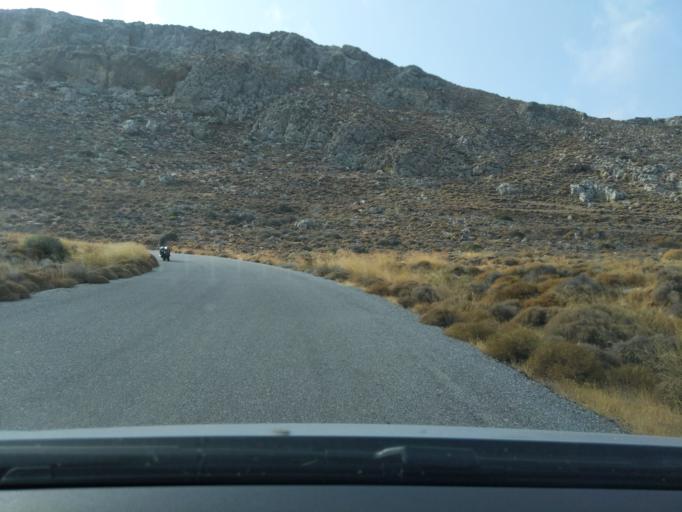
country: GR
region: Crete
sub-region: Nomos Lasithiou
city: Palekastro
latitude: 35.0902
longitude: 26.2619
